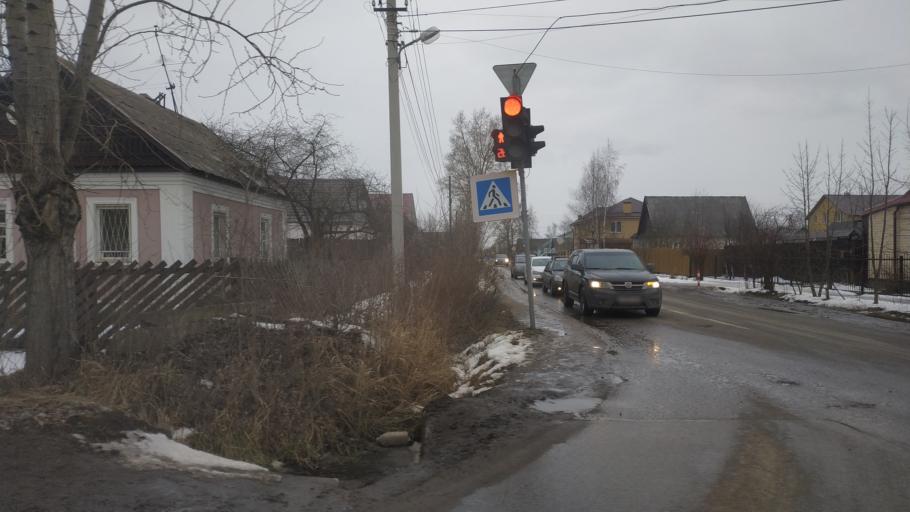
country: RU
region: Tverskaya
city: Tver
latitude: 56.8908
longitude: 35.8845
